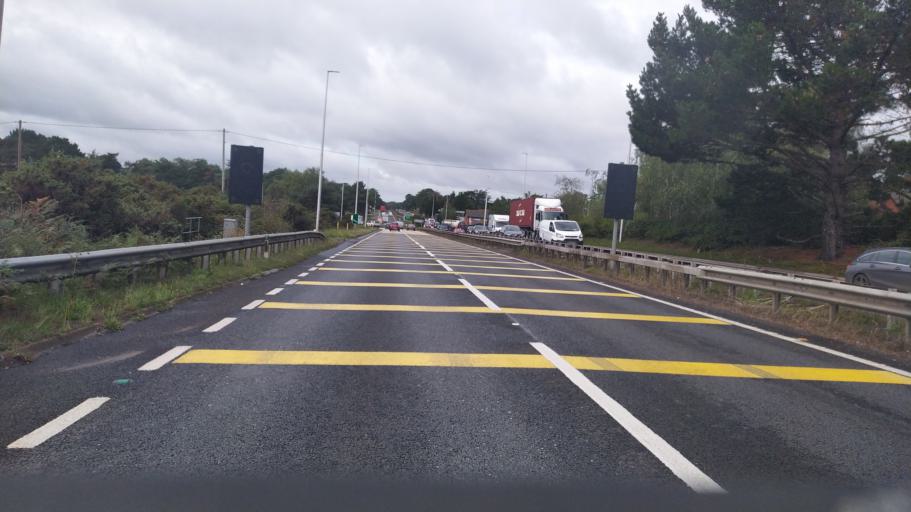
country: GB
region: England
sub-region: Dorset
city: St Leonards
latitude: 50.8303
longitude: -1.8350
